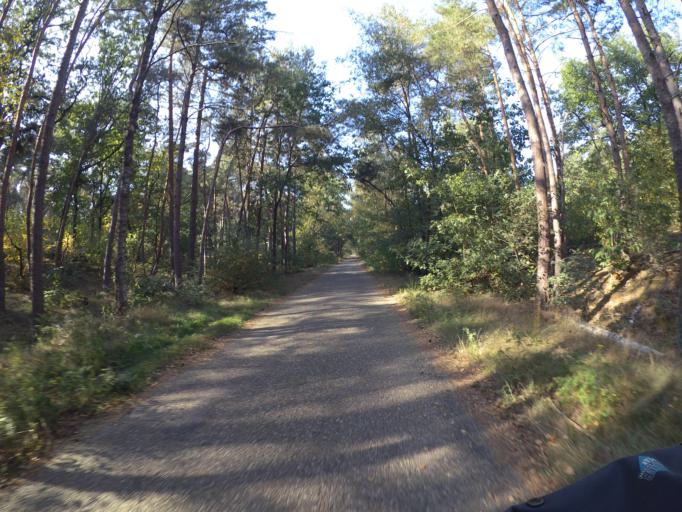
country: NL
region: North Brabant
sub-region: Gemeente Oirschot
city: Oirschot
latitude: 51.4701
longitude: 5.3325
